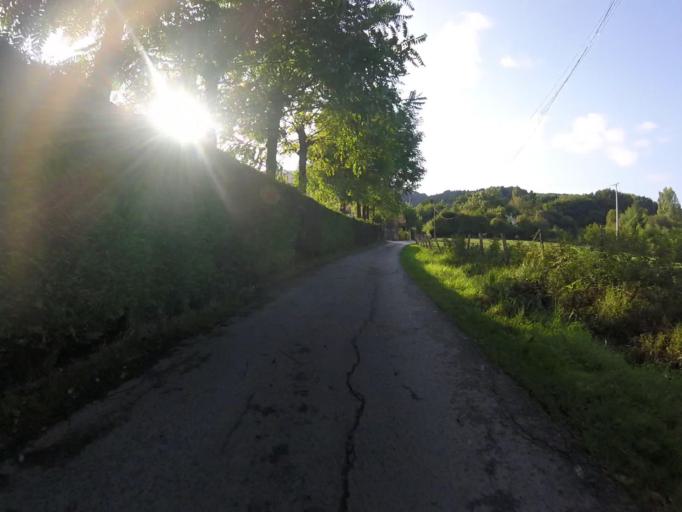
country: ES
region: Basque Country
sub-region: Provincia de Guipuzcoa
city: Fuenterrabia
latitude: 43.3597
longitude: -1.8125
